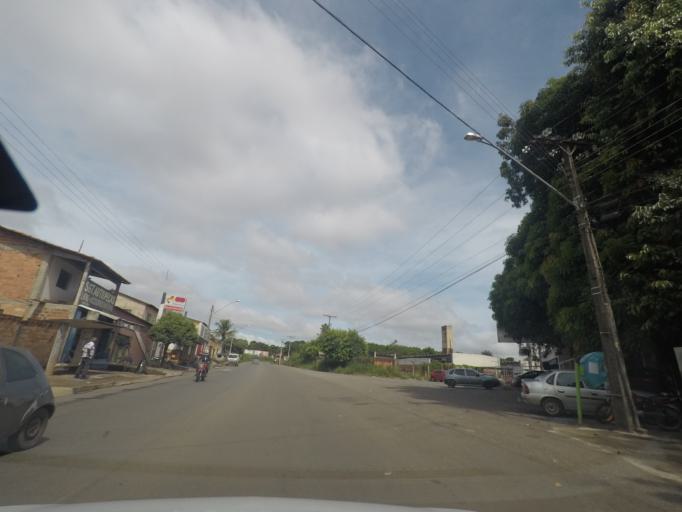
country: BR
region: Goias
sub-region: Goiania
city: Goiania
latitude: -16.6726
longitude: -49.2037
